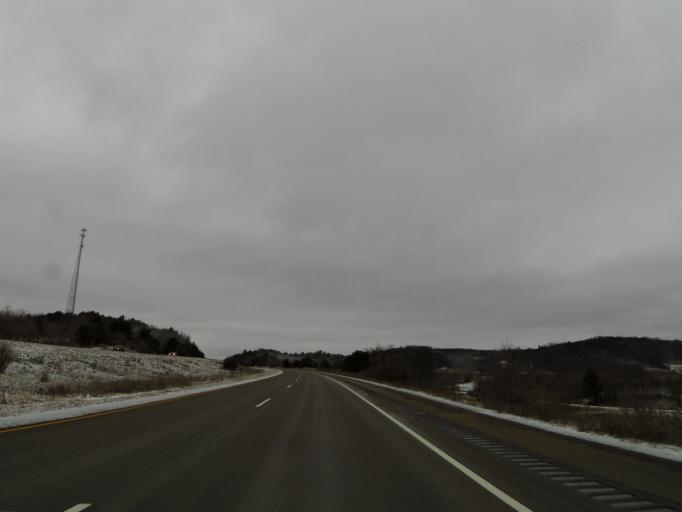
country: US
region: Wisconsin
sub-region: Trempealeau County
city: Osseo
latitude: 44.4987
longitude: -91.1244
